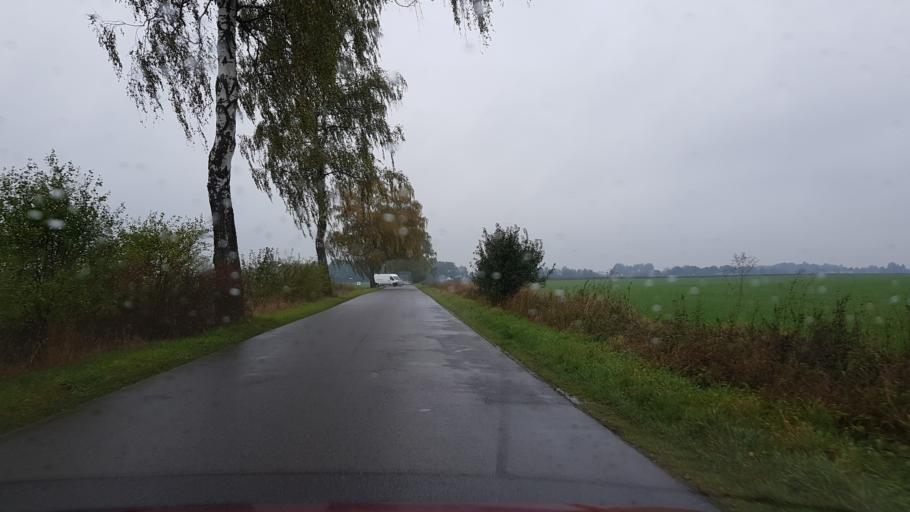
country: PL
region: Greater Poland Voivodeship
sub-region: Powiat zlotowski
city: Krajenka
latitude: 53.3219
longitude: 16.9376
